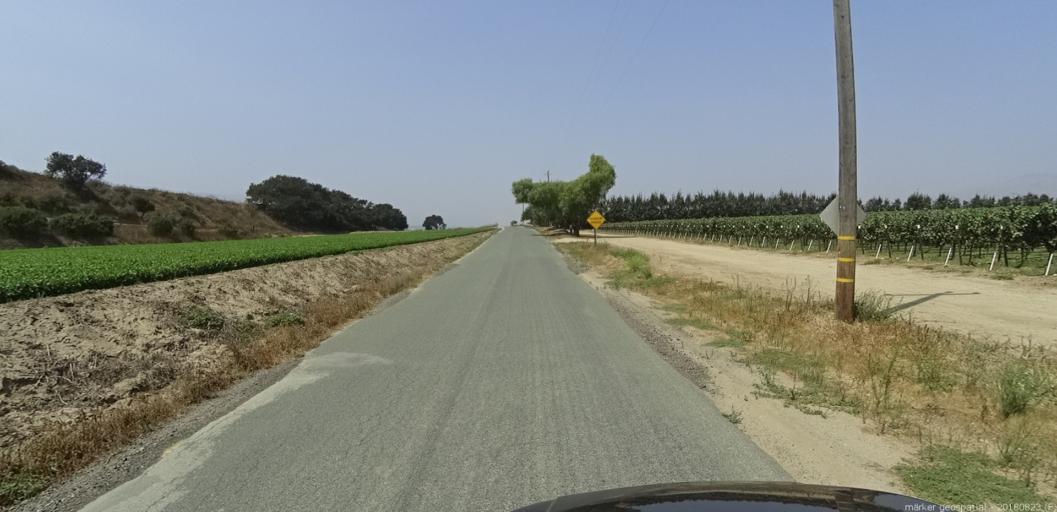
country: US
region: California
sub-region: Monterey County
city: Soledad
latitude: 36.3708
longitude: -121.3175
